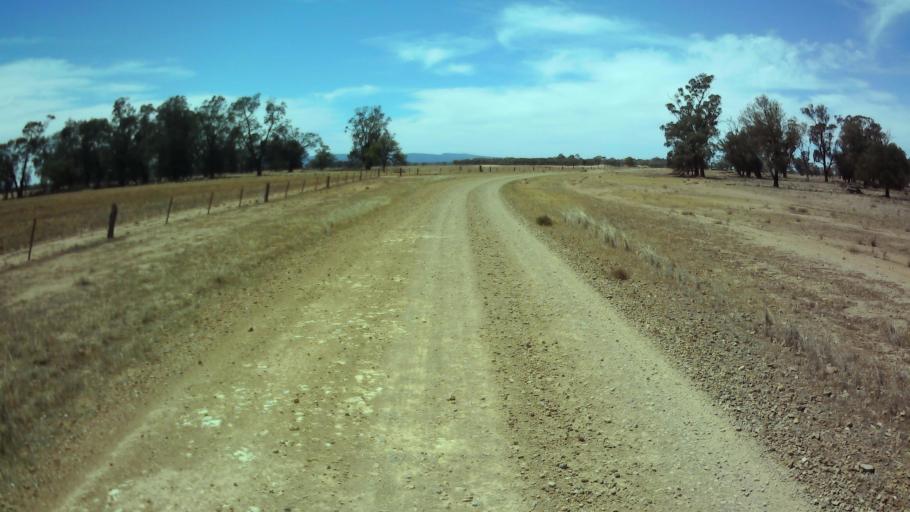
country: AU
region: New South Wales
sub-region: Weddin
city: Grenfell
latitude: -33.8626
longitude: 147.7585
